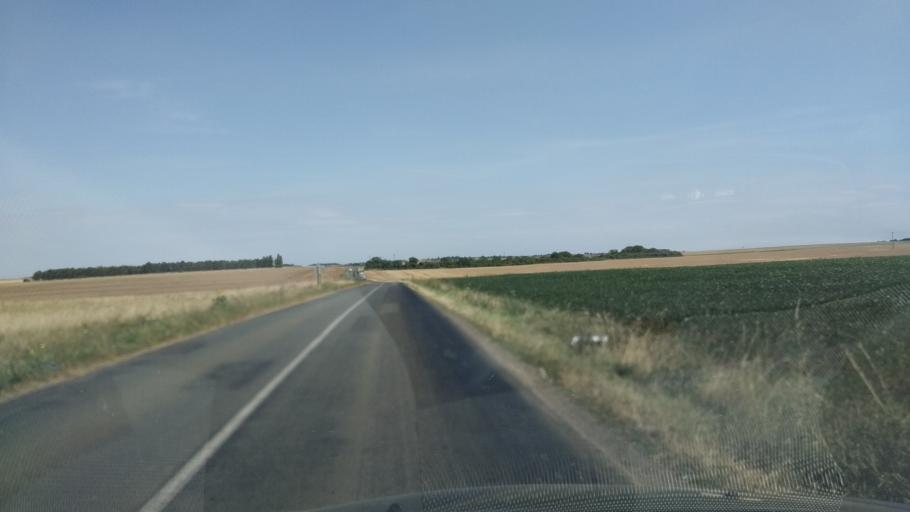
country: FR
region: Poitou-Charentes
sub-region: Departement de la Vienne
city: Vouille
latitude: 46.6730
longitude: 0.1903
